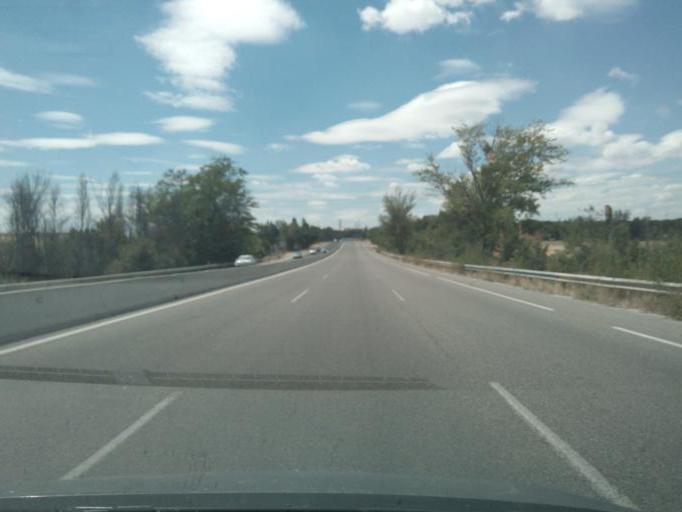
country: ES
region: Madrid
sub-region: Provincia de Madrid
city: San Sebastian de los Reyes
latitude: 40.5775
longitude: -3.5901
